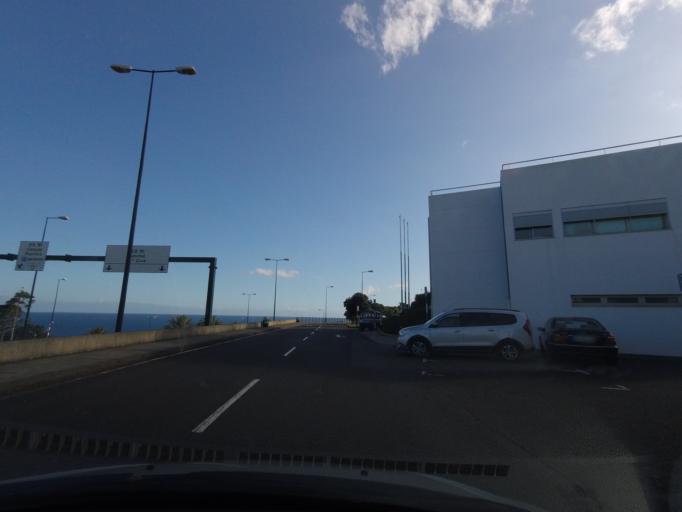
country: PT
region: Madeira
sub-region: Machico
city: Machico
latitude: 32.6923
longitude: -16.7766
